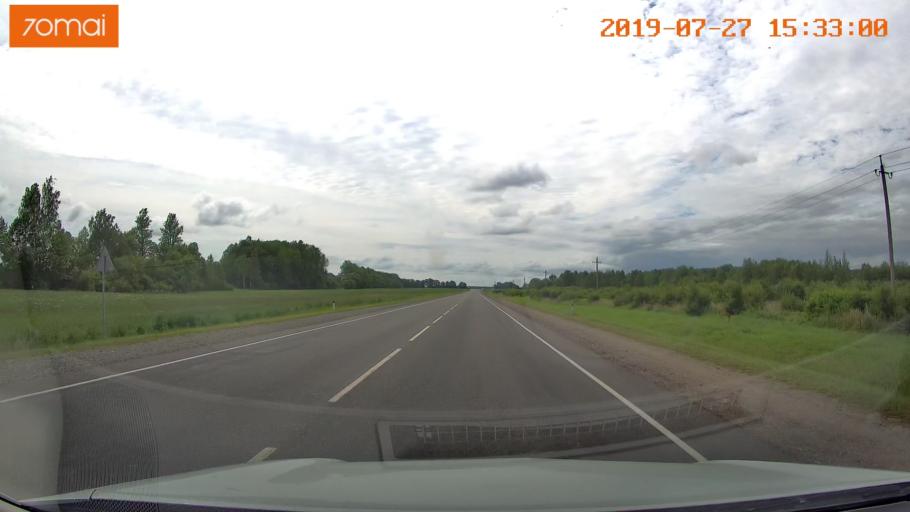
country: RU
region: Kaliningrad
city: Nesterov
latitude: 54.6146
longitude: 22.4613
